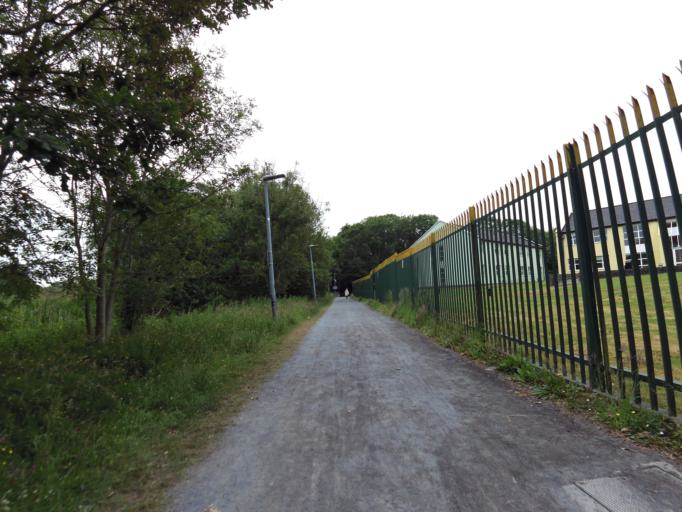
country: IE
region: Connaught
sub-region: County Galway
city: Gaillimh
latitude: 53.2863
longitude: -9.0646
